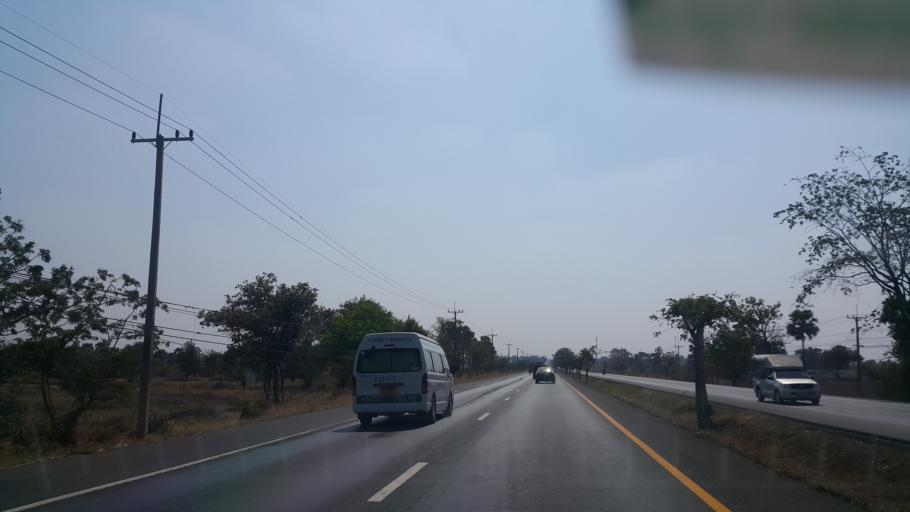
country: TH
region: Nakhon Ratchasima
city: Non Daeng
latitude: 15.4260
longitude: 102.4862
